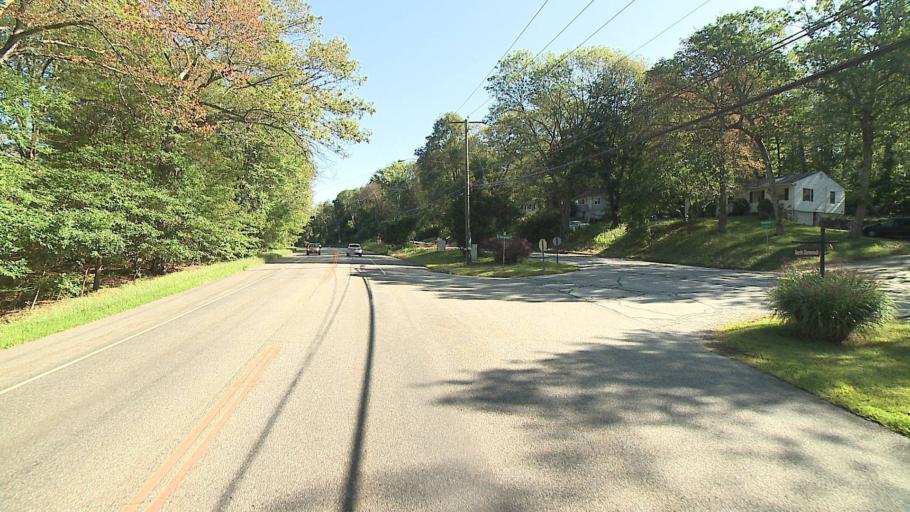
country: US
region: Connecticut
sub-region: New London County
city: Gales Ferry
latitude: 41.4615
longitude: -72.0619
